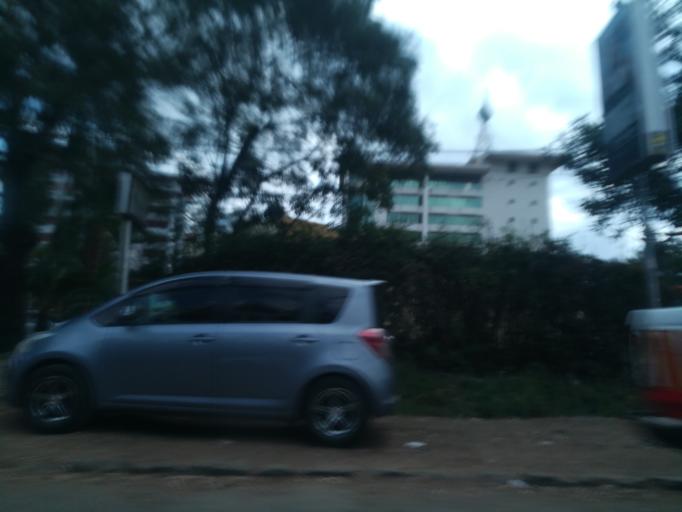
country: KE
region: Nairobi Area
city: Nairobi
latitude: -1.2924
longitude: 36.7907
